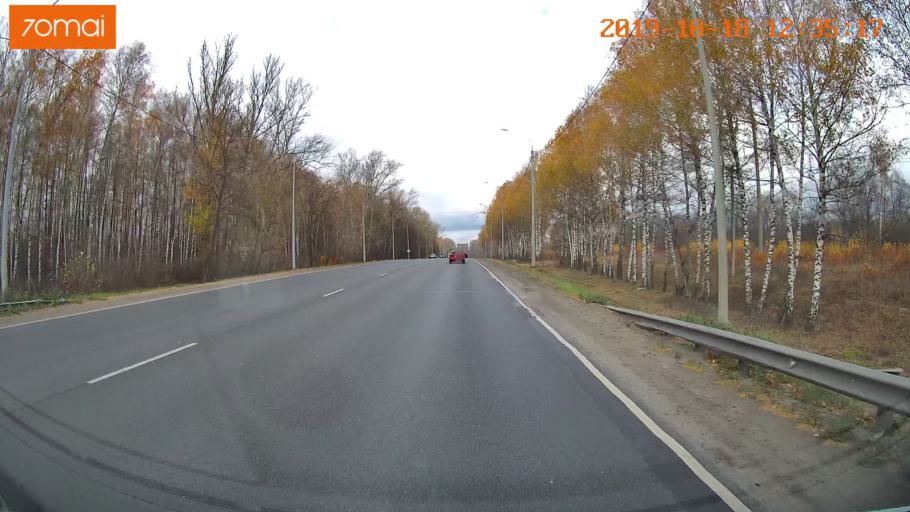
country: RU
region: Rjazan
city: Ryazan'
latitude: 54.6228
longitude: 39.6360
